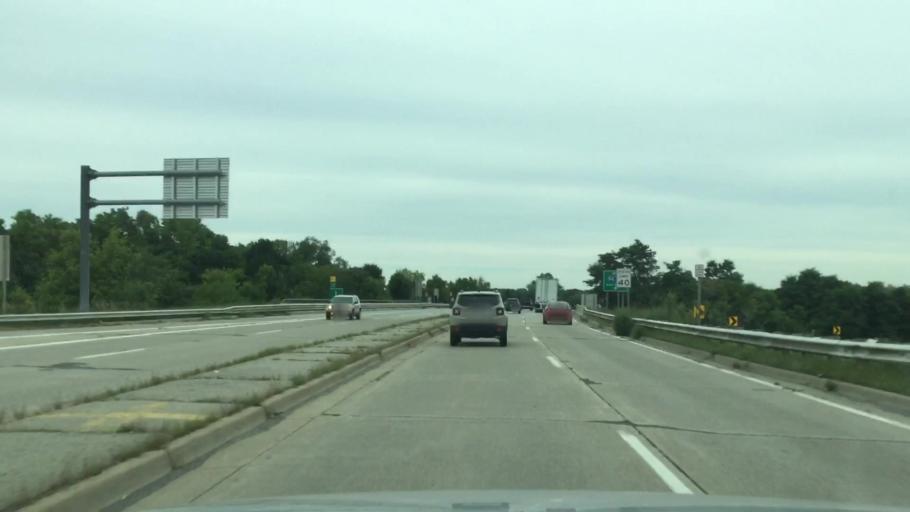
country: US
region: Michigan
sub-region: Washtenaw County
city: Ypsilanti
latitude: 42.2278
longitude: -83.6172
